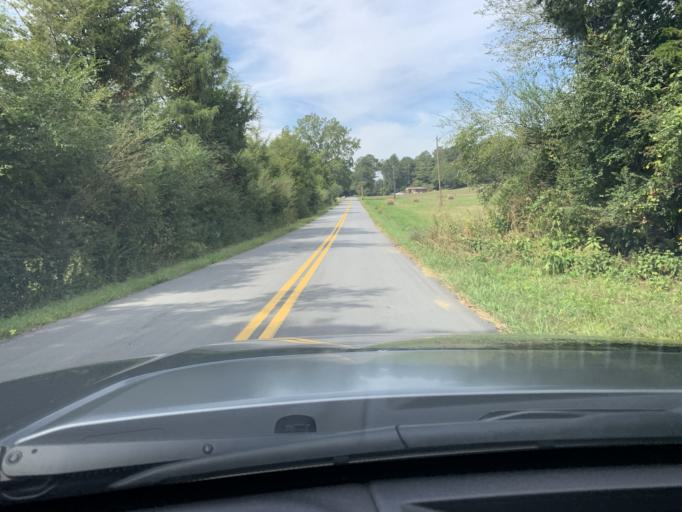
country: US
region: Georgia
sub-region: Polk County
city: Cedartown
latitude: 33.9472
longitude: -85.3734
